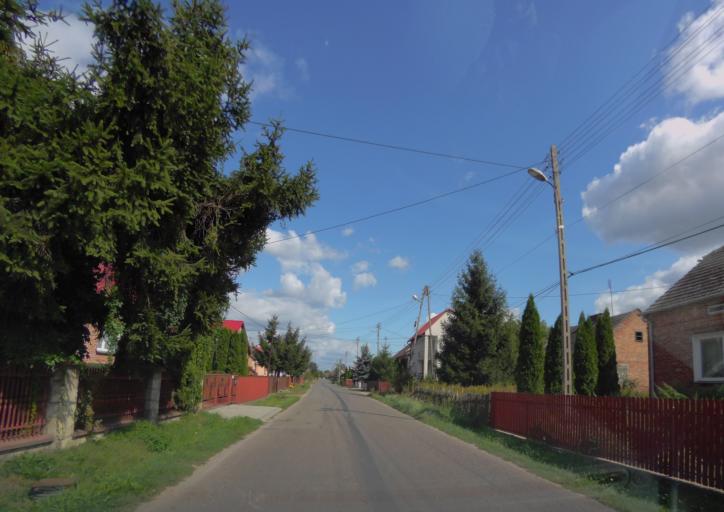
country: PL
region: Subcarpathian Voivodeship
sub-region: Tarnobrzeg
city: Tarnobrzeg
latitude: 50.5125
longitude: 21.6635
